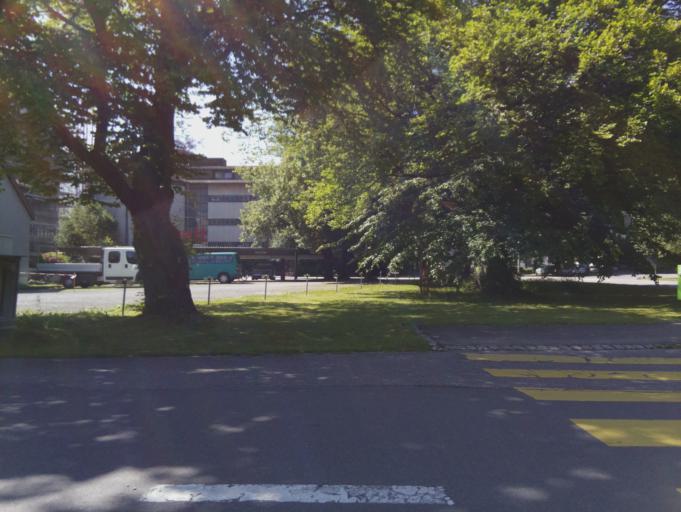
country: CH
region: Glarus
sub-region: Glarus
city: Niederurnen
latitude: 47.1229
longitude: 9.0585
